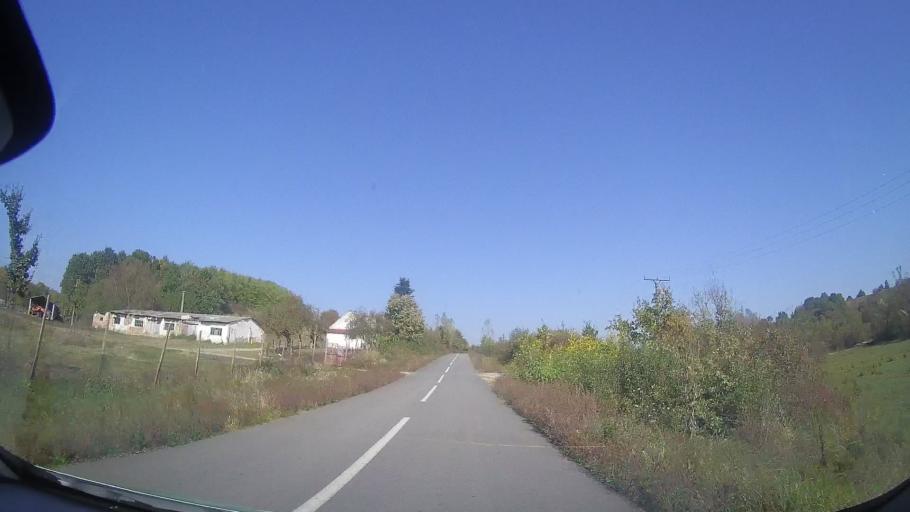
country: RO
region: Timis
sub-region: Comuna Bara
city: Bara
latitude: 45.8767
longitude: 21.8850
